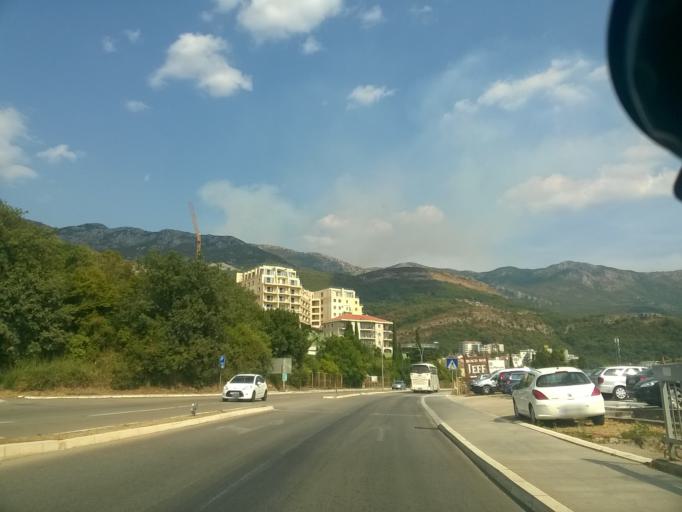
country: ME
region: Budva
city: Budva
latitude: 42.2835
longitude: 18.8715
